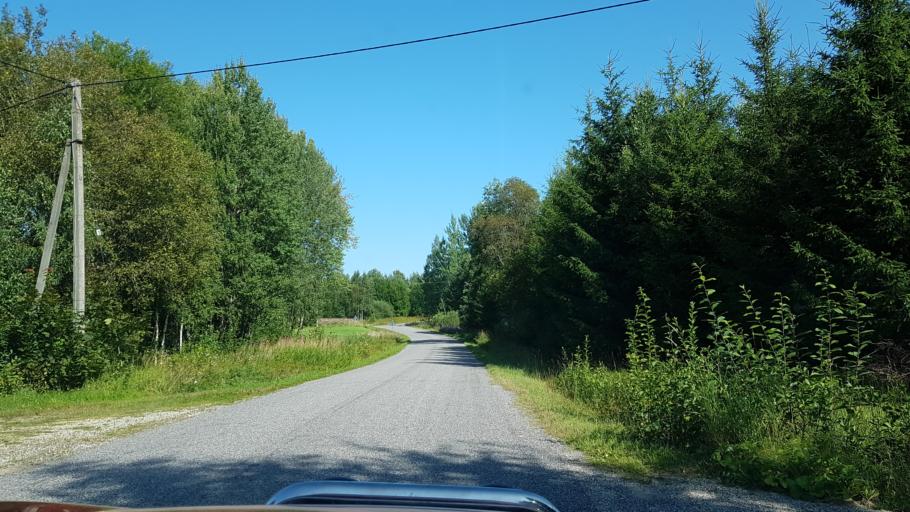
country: EE
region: Vorumaa
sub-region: Voru linn
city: Voru
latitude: 57.7064
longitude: 27.1904
